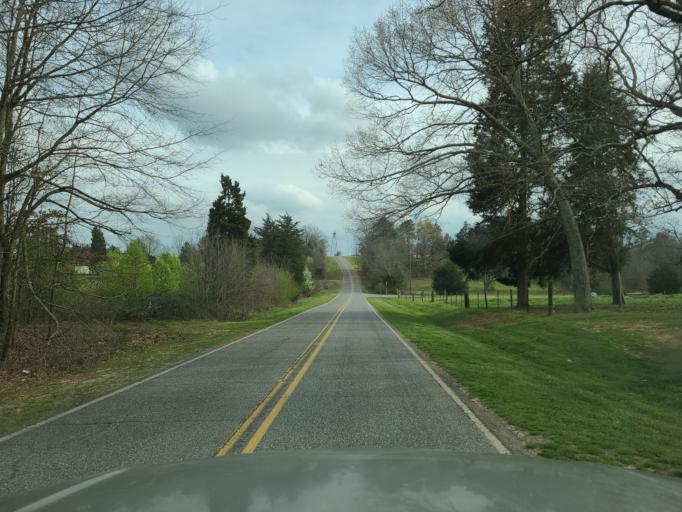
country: US
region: North Carolina
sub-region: Cleveland County
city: Boiling Springs
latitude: 35.2383
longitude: -81.7382
